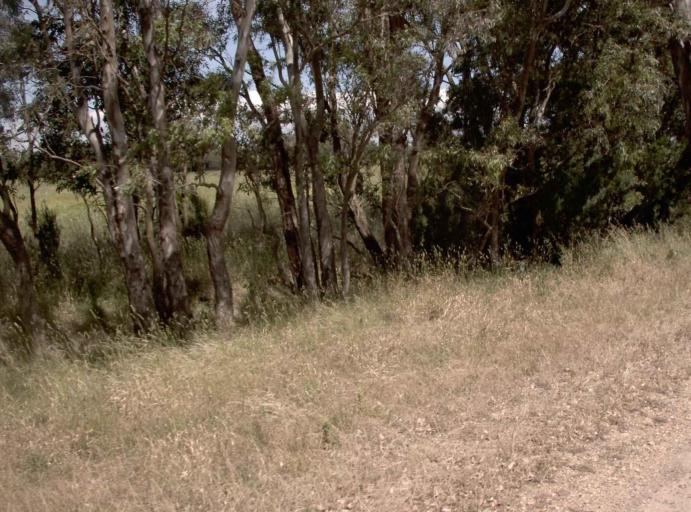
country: AU
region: Victoria
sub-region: Wellington
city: Heyfield
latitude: -38.0045
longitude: 146.8835
